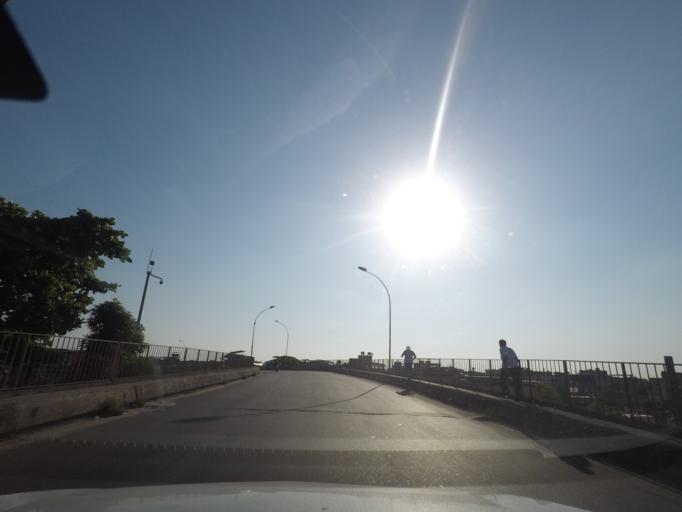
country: BR
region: Rio de Janeiro
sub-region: Rio De Janeiro
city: Rio de Janeiro
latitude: -22.8509
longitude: -43.2479
